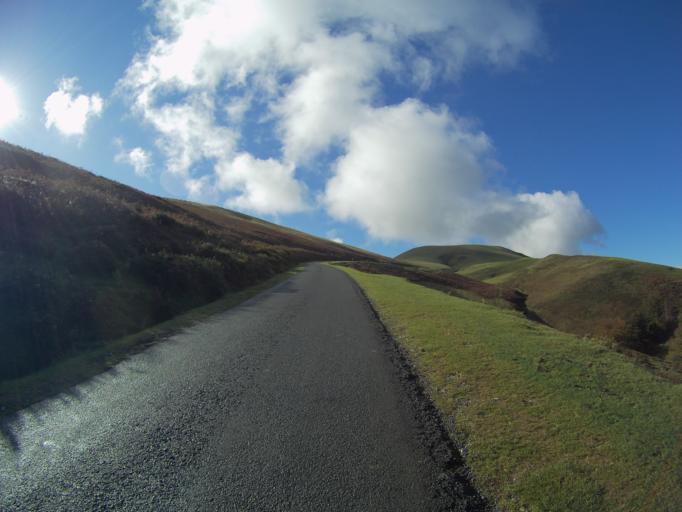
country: FR
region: Aquitaine
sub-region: Departement des Pyrenees-Atlantiques
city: Saint-Jean-Pied-de-Port
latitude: 43.0947
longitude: -1.2427
